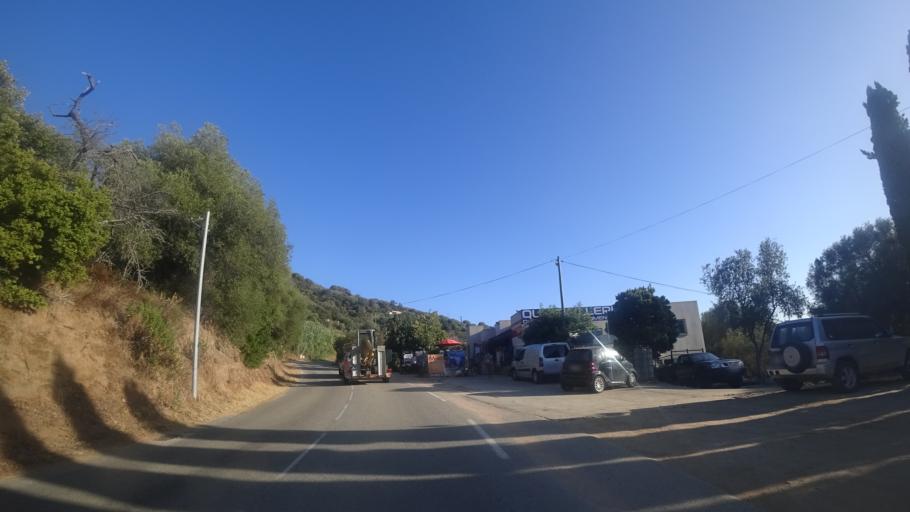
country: FR
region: Corsica
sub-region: Departement de la Corse-du-Sud
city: Cargese
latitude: 42.1446
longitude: 8.6026
